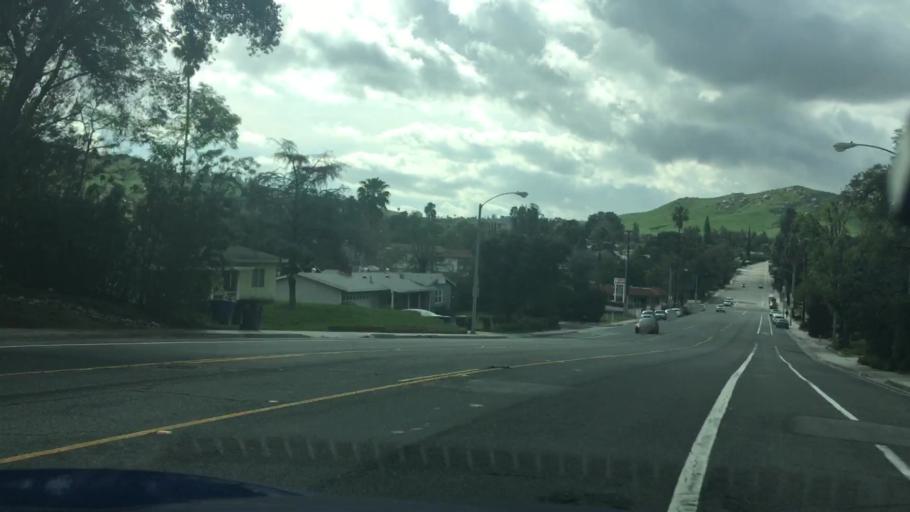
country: US
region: California
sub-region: Riverside County
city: Highgrove
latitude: 33.9780
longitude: -117.3165
